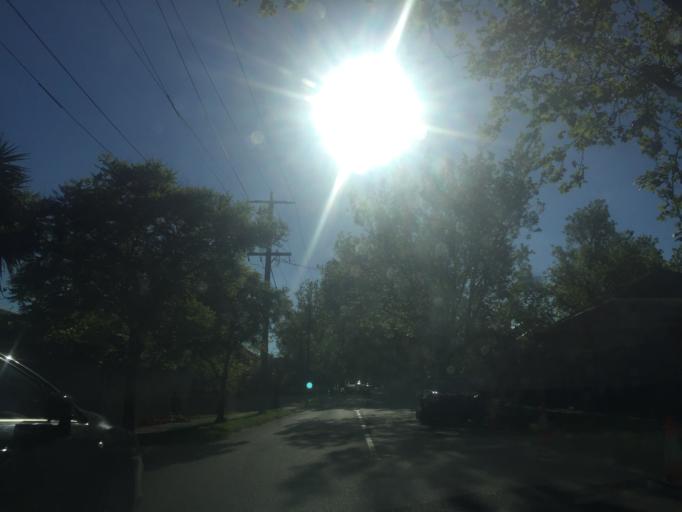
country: AU
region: Victoria
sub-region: Boroondara
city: Canterbury
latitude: -37.8172
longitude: 145.0829
